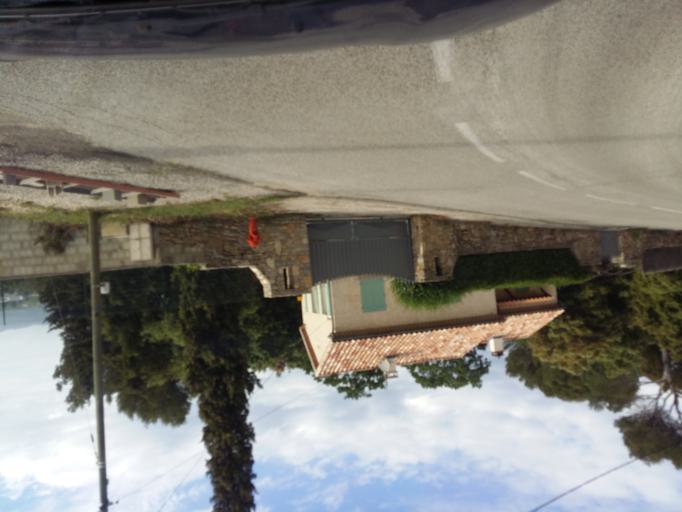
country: FR
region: Languedoc-Roussillon
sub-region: Departement du Gard
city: Bagnols-sur-Ceze
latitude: 44.1451
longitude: 4.6134
